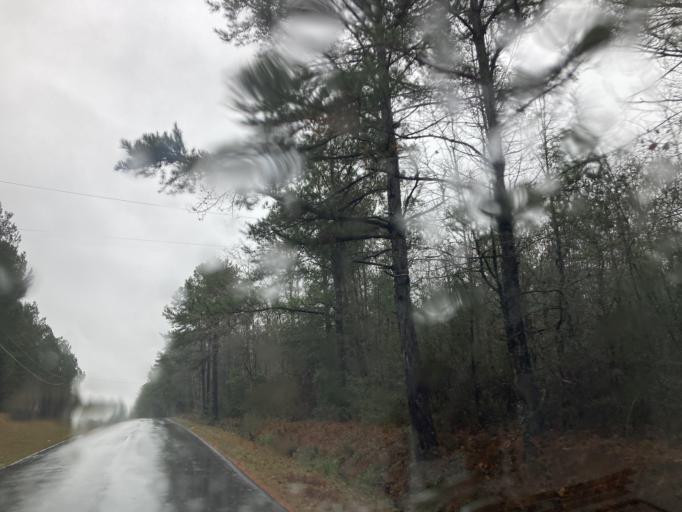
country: US
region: Mississippi
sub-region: Forrest County
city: Rawls Springs
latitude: 31.4756
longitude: -89.3822
